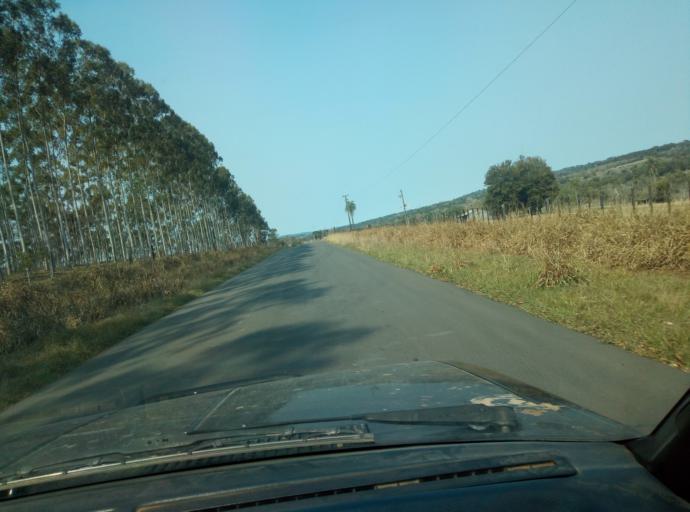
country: PY
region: Caaguazu
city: Carayao
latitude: -25.2549
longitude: -56.2880
